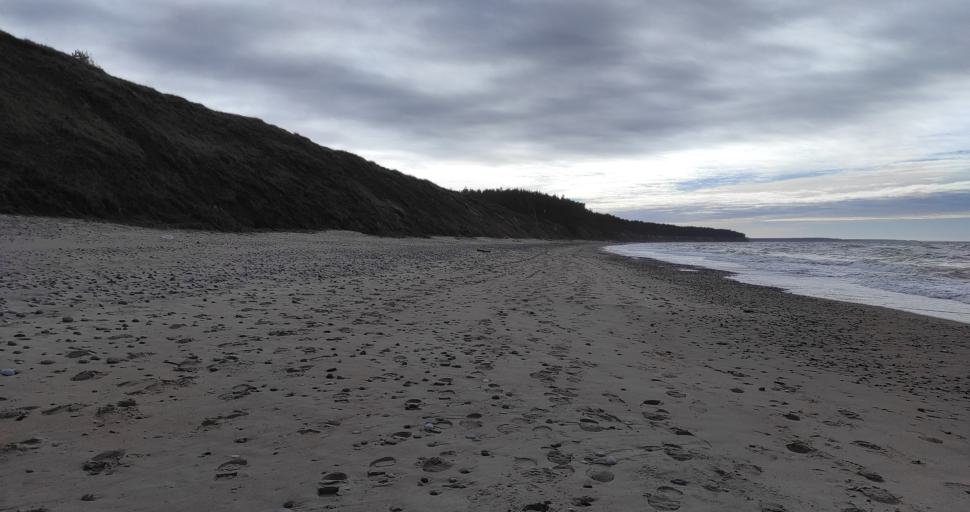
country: LV
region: Alsunga
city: Alsunga
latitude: 57.0363
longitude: 21.4012
